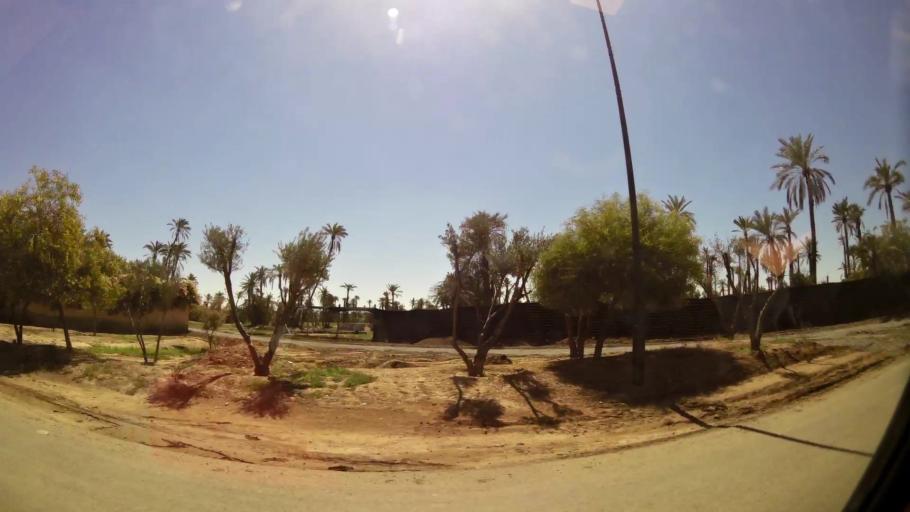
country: MA
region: Marrakech-Tensift-Al Haouz
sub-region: Marrakech
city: Marrakesh
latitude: 31.6684
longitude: -7.9850
